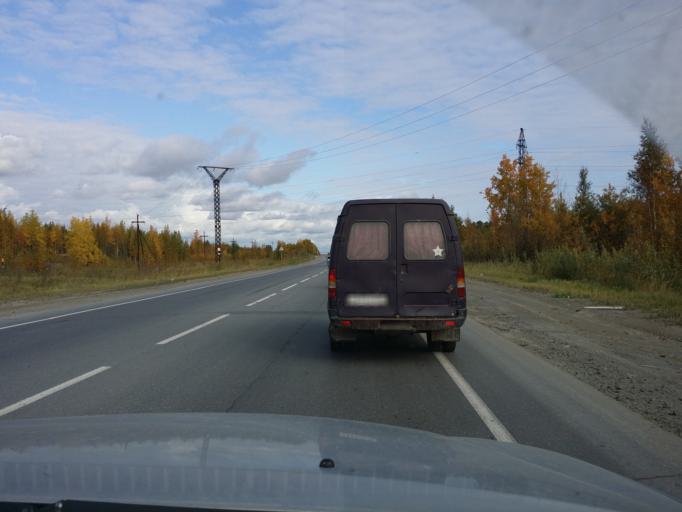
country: RU
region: Khanty-Mansiyskiy Avtonomnyy Okrug
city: Megion
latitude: 61.0585
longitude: 76.1144
